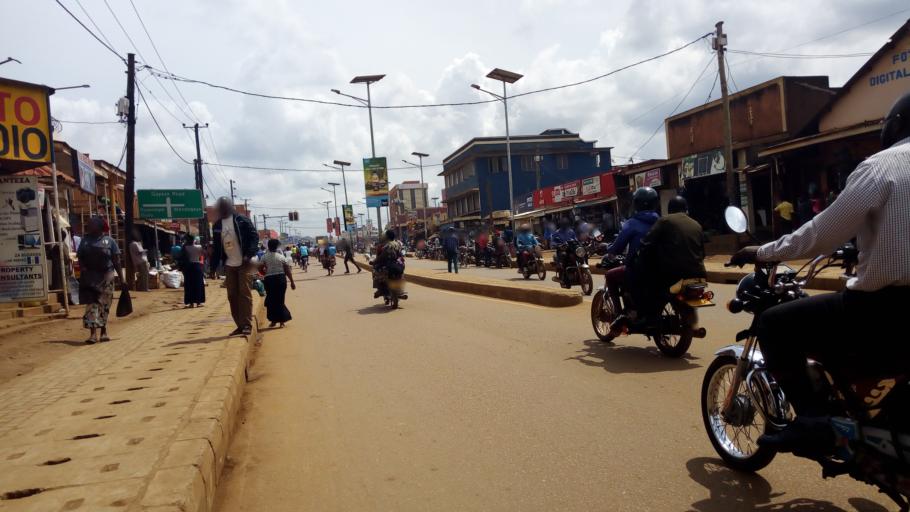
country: UG
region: Central Region
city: Kampala Central Division
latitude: 0.3528
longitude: 32.5614
